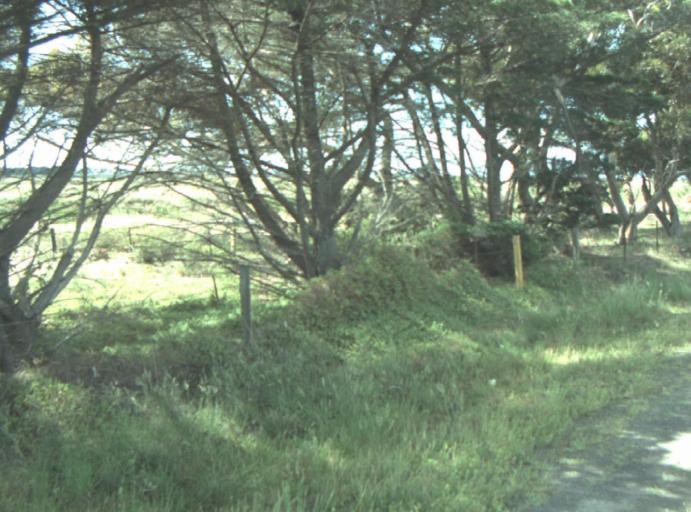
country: AU
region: Victoria
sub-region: Greater Geelong
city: Lara
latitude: -38.0513
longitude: 144.4284
